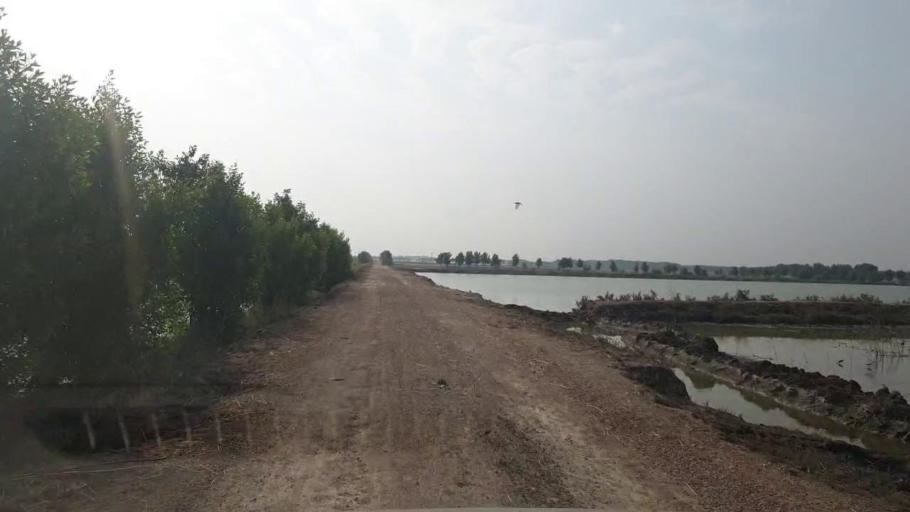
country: PK
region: Sindh
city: Tando Muhammad Khan
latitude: 25.0989
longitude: 68.5071
